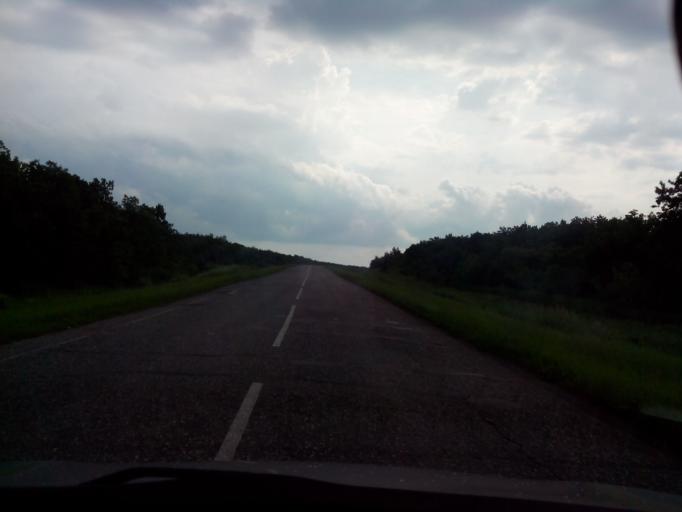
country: RU
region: Volgograd
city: Kumylzhenskaya
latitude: 49.9073
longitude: 42.8638
